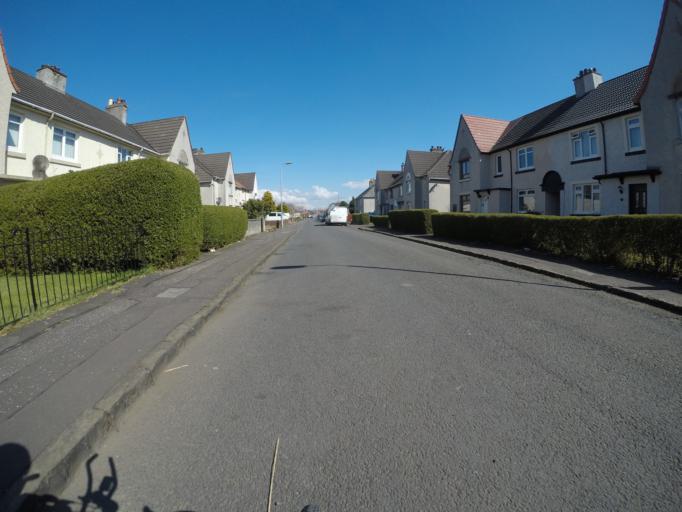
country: GB
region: Scotland
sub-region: North Ayrshire
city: Irvine
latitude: 55.6163
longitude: -4.6570
